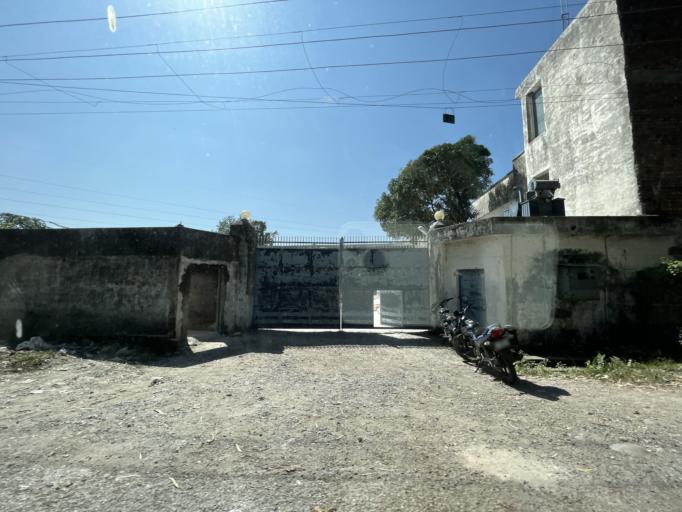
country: IN
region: Uttarakhand
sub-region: Naini Tal
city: Haldwani
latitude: 29.2115
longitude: 79.4607
